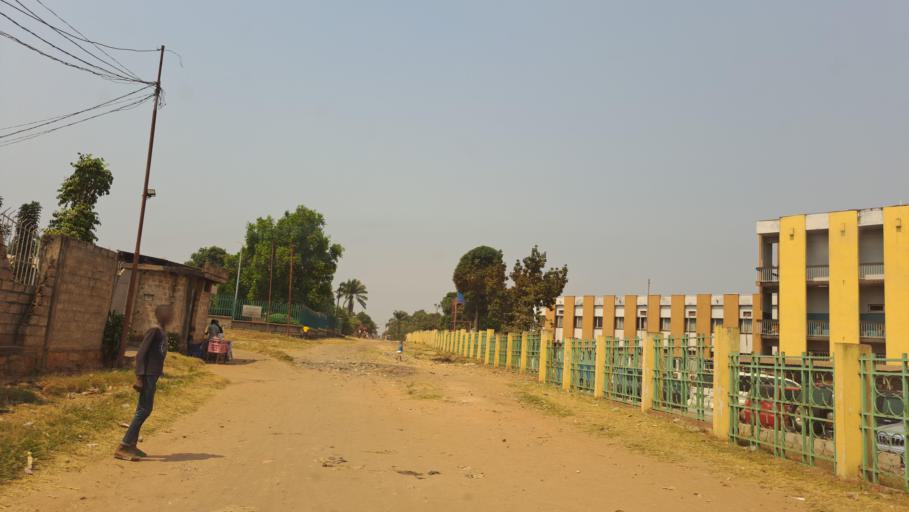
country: CD
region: Kasai-Oriental
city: Mbuji-Mayi
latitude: -6.1098
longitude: 23.5948
